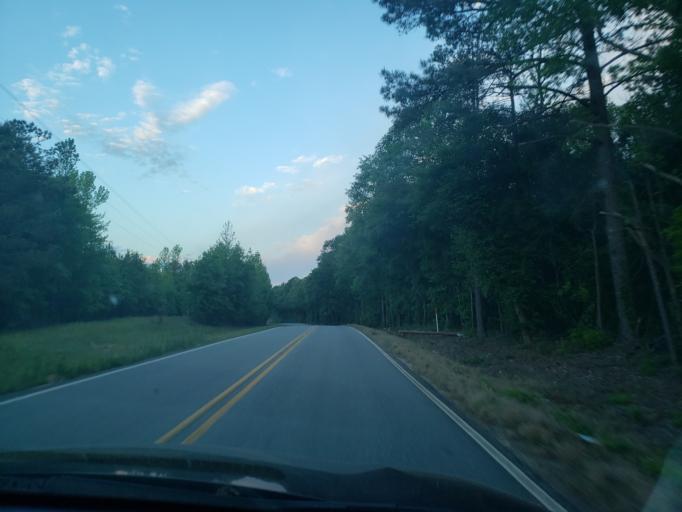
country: US
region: Alabama
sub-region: Tallapoosa County
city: Camp Hill
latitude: 32.7003
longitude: -85.6579
